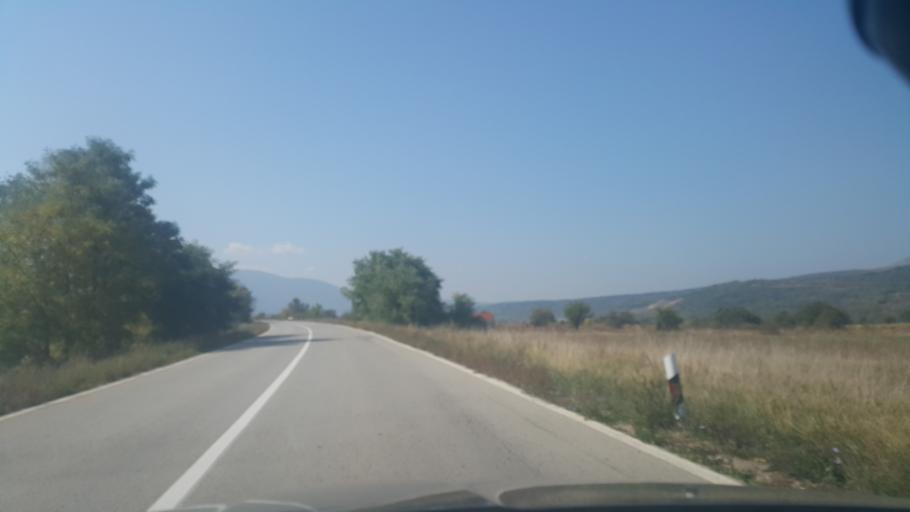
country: RS
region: Central Serbia
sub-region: Pirotski Okrug
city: Bela Palanka
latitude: 43.2272
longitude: 22.3767
